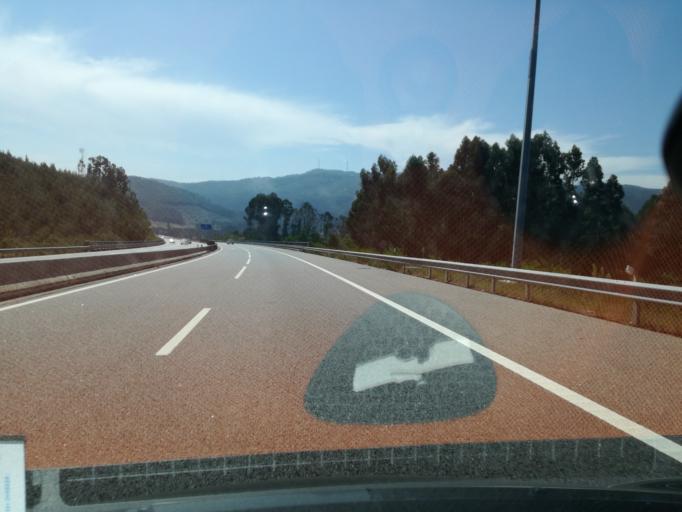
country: PT
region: Viana do Castelo
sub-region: Caminha
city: Vila Praia de Ancora
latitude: 41.8116
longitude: -8.8054
